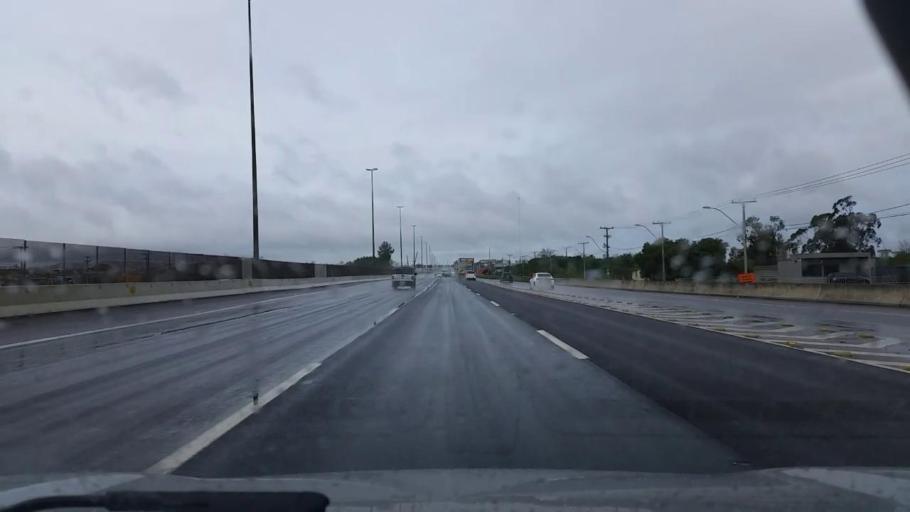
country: BR
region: Rio Grande do Sul
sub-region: Porto Alegre
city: Porto Alegre
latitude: -29.9780
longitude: -51.2004
